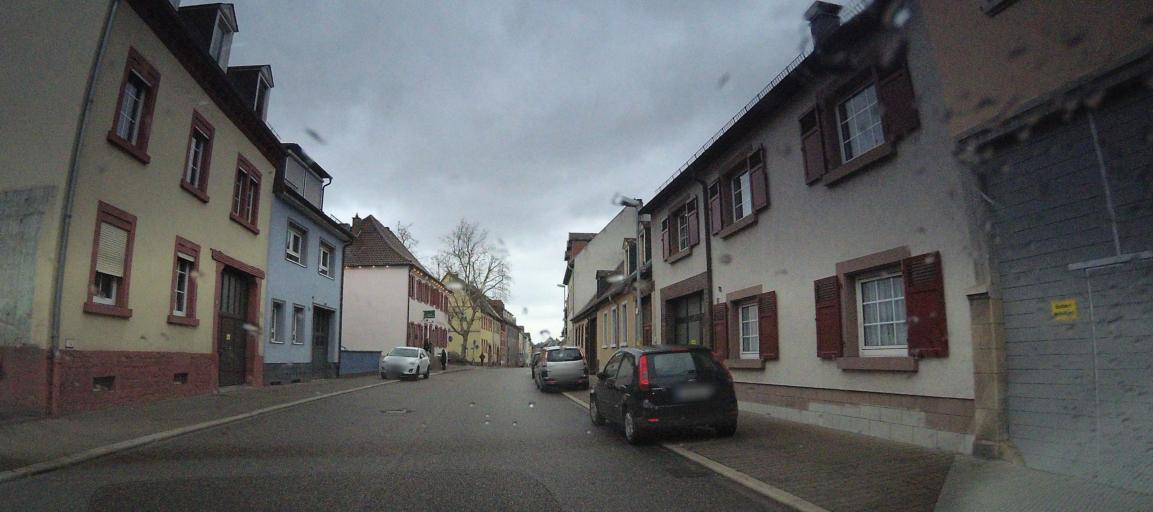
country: DE
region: Baden-Wuerttemberg
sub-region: Karlsruhe Region
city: Bruchsal
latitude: 49.1211
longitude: 8.6053
